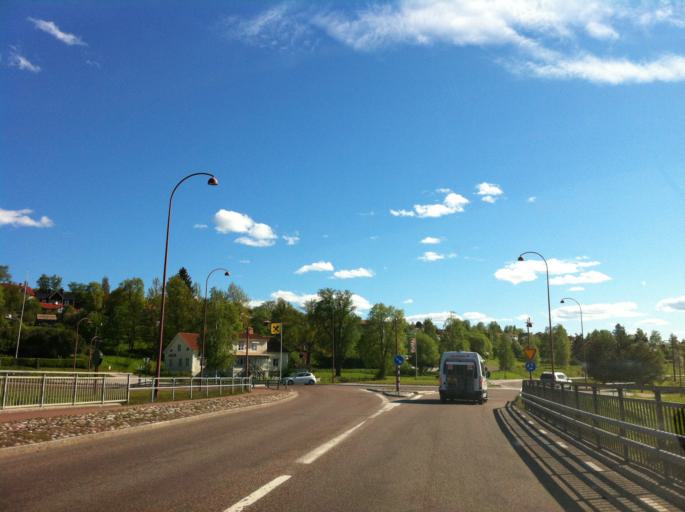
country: SE
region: Dalarna
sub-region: Rattviks Kommun
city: Raettvik
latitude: 60.8814
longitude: 15.1187
